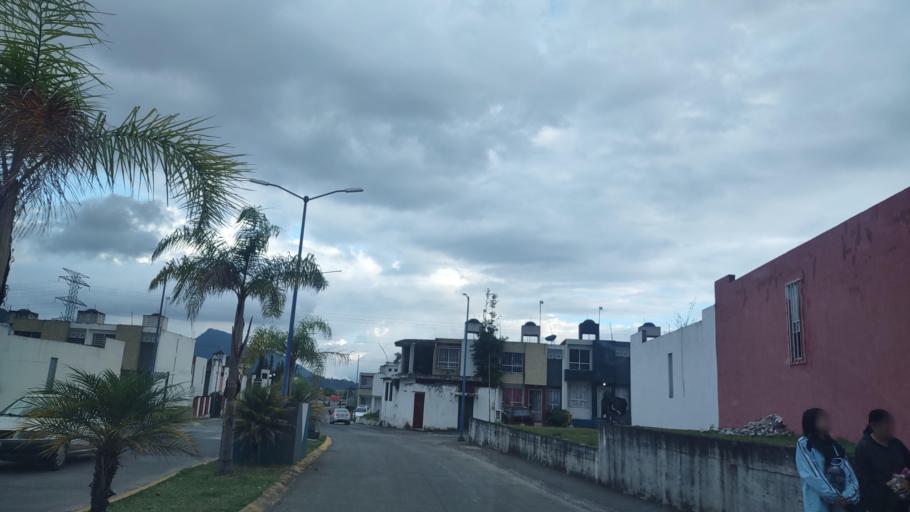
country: MX
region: Veracruz
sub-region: Ixtaczoquitlan
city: Buenavista
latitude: 18.8829
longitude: -97.0596
